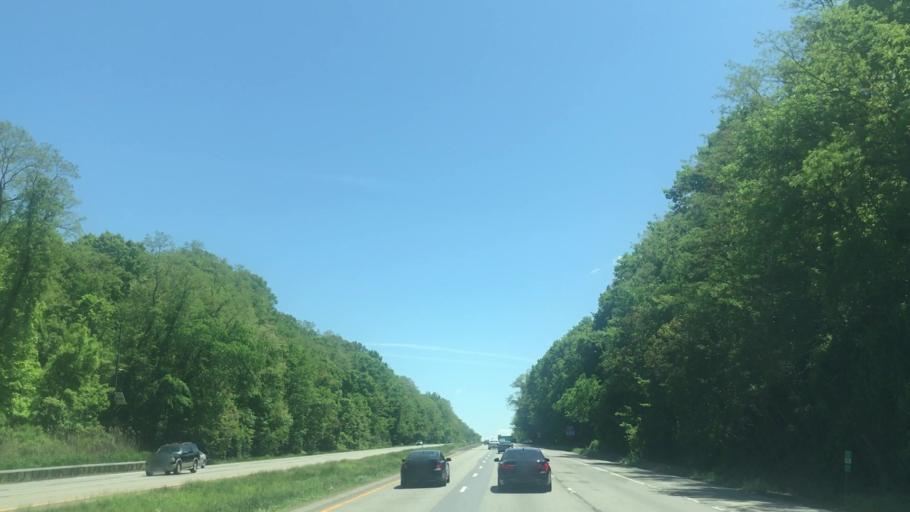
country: US
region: New York
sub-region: Westchester County
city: Purchase
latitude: 41.0526
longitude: -73.7282
